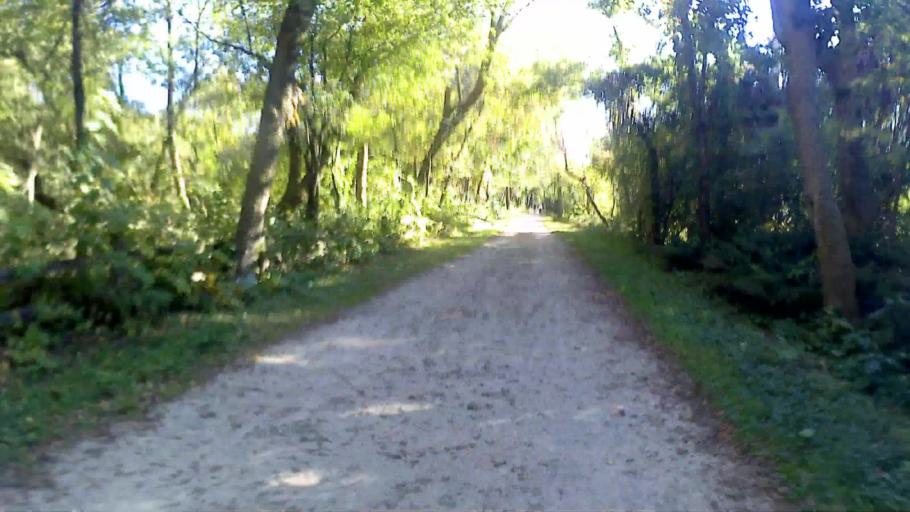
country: US
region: Illinois
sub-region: DuPage County
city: Wheaton
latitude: 41.8577
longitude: -88.1163
